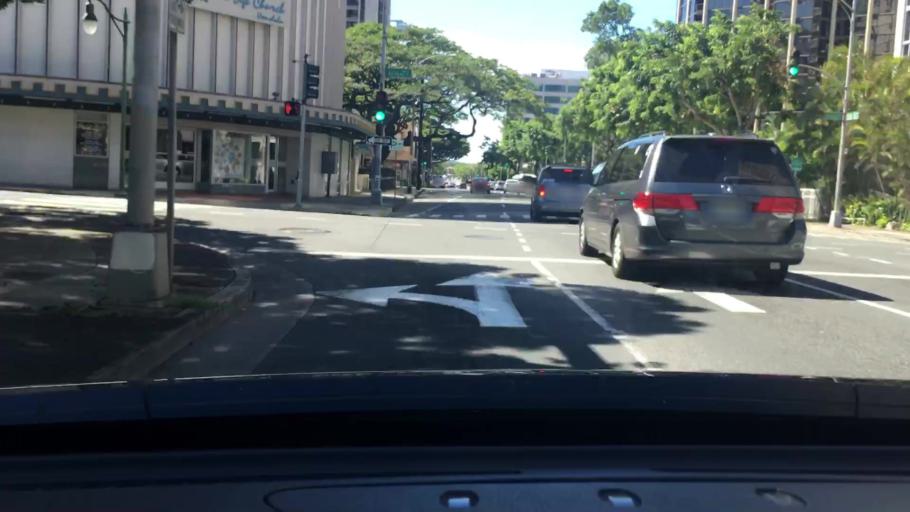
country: US
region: Hawaii
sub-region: Honolulu County
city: Honolulu
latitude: 21.3120
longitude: -157.8601
